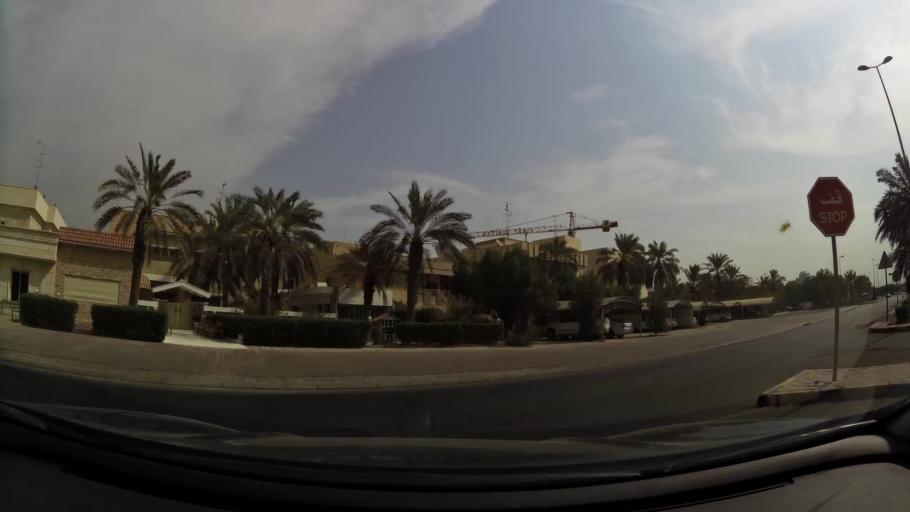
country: KW
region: Al Asimah
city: Ash Shamiyah
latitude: 29.3463
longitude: 47.9794
